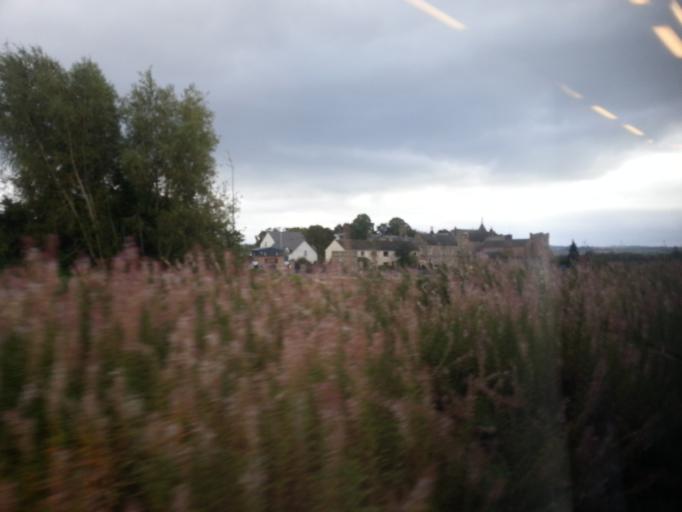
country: GB
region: Scotland
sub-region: Highland
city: Dingwall
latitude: 57.5963
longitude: -4.4213
